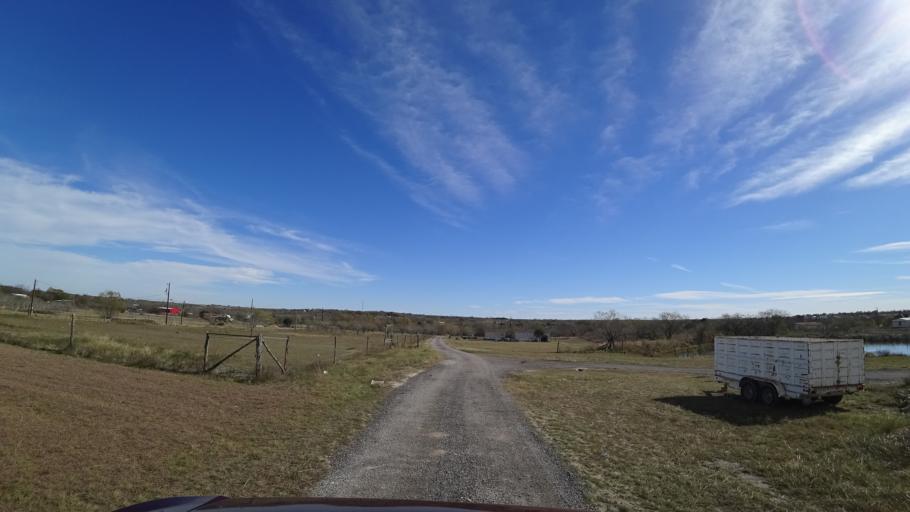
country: US
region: Texas
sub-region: Travis County
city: Onion Creek
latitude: 30.1187
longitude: -97.7190
